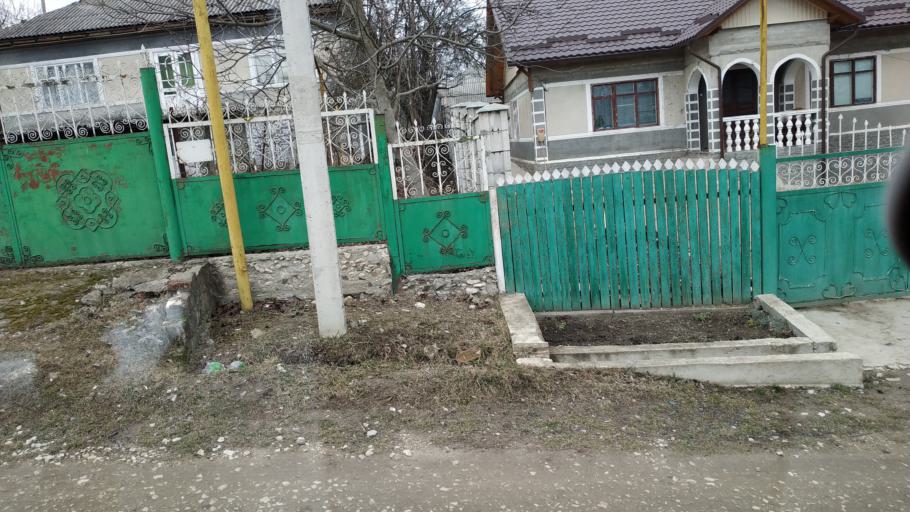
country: MD
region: Calarasi
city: Calarasi
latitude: 47.2363
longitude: 28.3103
